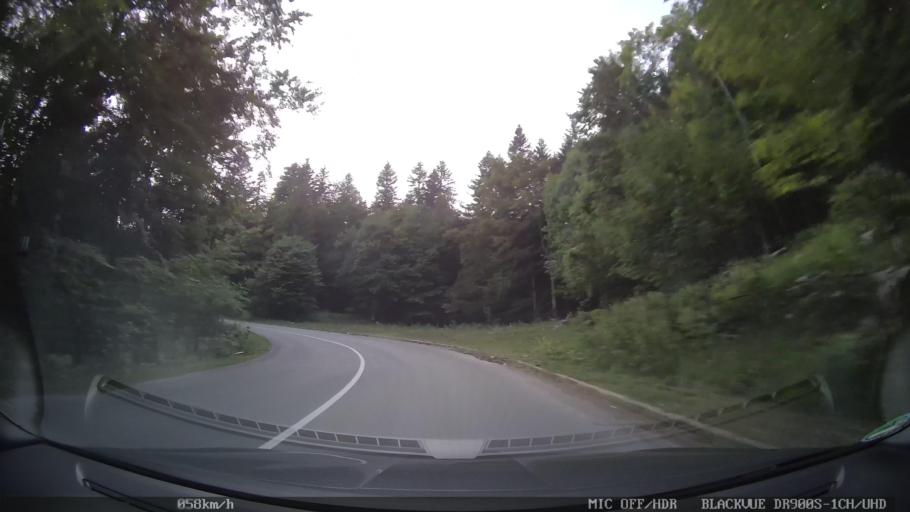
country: HR
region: Primorsko-Goranska
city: Novi Vinodolski
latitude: 45.1654
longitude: 14.9466
